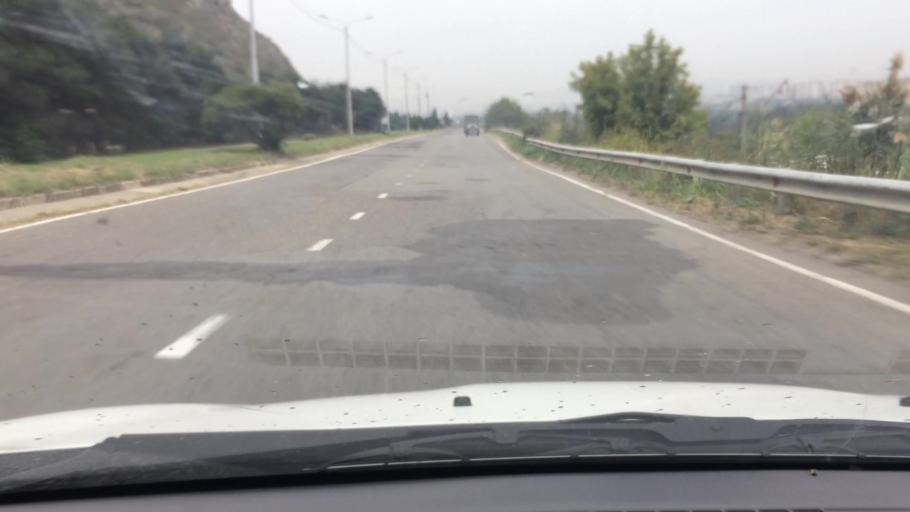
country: GE
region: T'bilisi
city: Tbilisi
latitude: 41.6561
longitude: 44.8957
